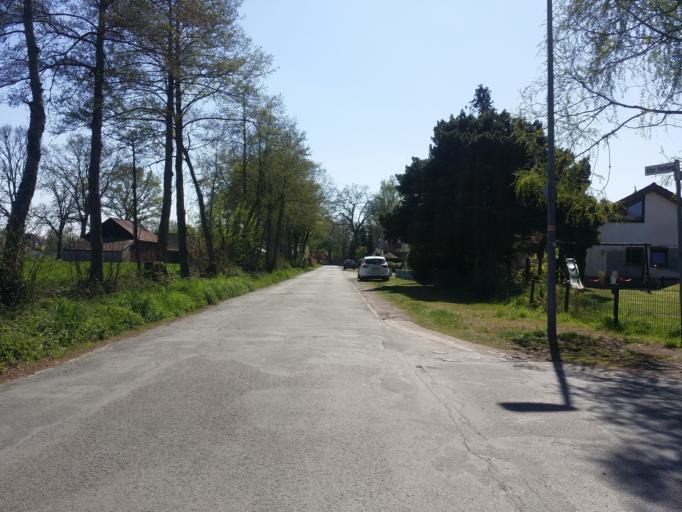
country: DE
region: Lower Saxony
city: Stuhr
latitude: 53.0275
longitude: 8.6892
